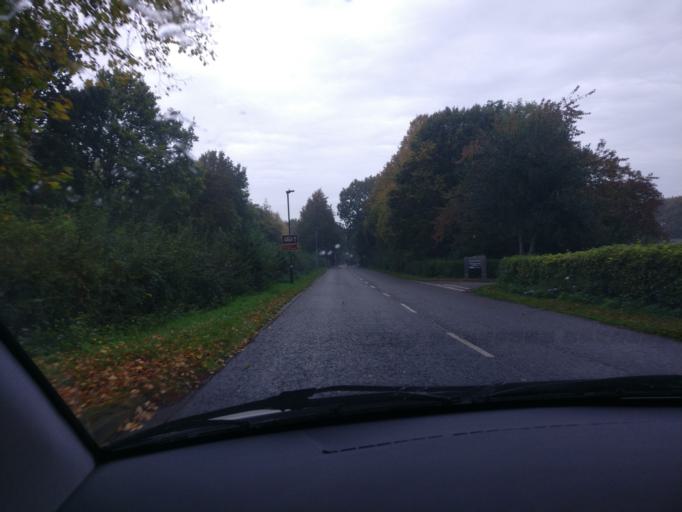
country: GB
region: England
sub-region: Peterborough
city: Castor
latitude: 52.5576
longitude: -0.3025
